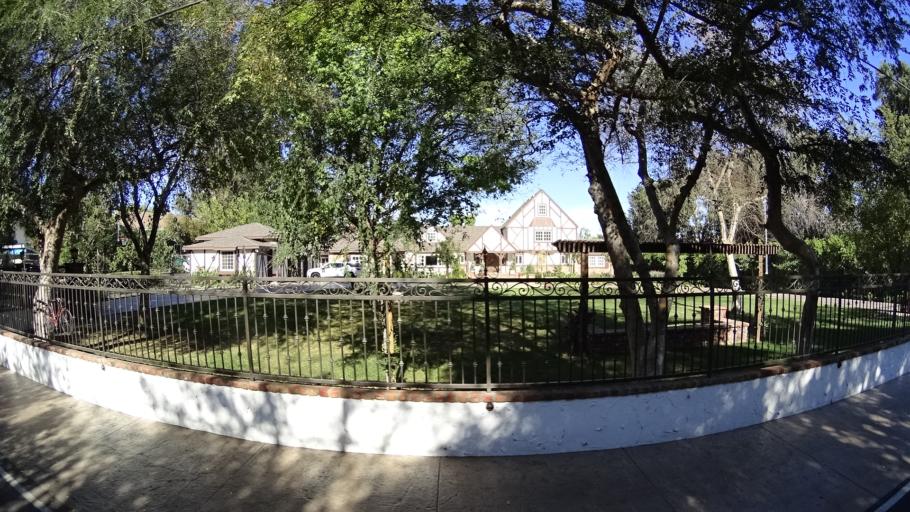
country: US
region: California
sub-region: Orange County
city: Villa Park
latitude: 33.8095
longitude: -117.7868
